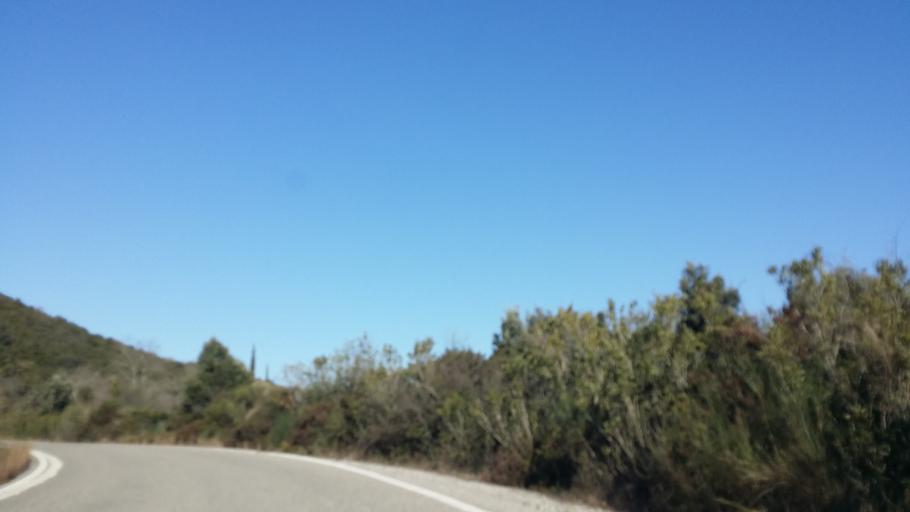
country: GR
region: West Greece
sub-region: Nomos Aitolias kai Akarnanias
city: Lepenou
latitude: 38.7693
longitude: 21.3364
